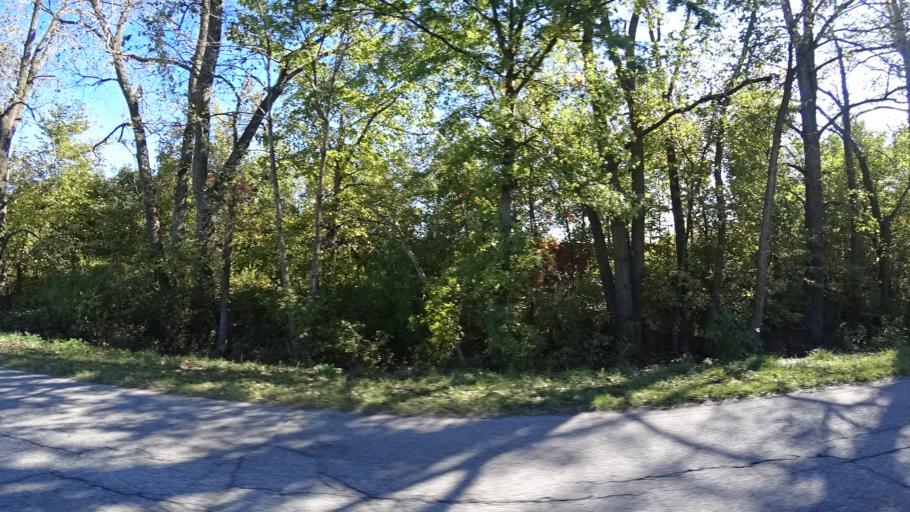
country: US
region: Indiana
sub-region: LaPorte County
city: Michigan City
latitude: 41.6749
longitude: -86.9134
